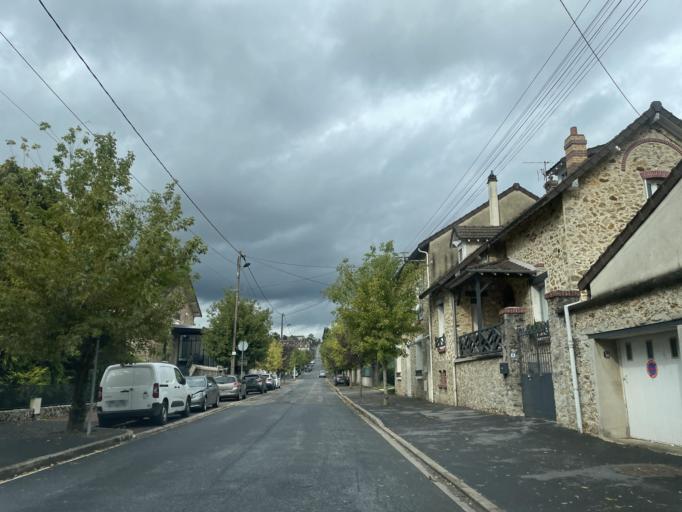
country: FR
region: Ile-de-France
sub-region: Departement de Seine-et-Marne
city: Coulommiers
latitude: 48.8185
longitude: 3.0851
